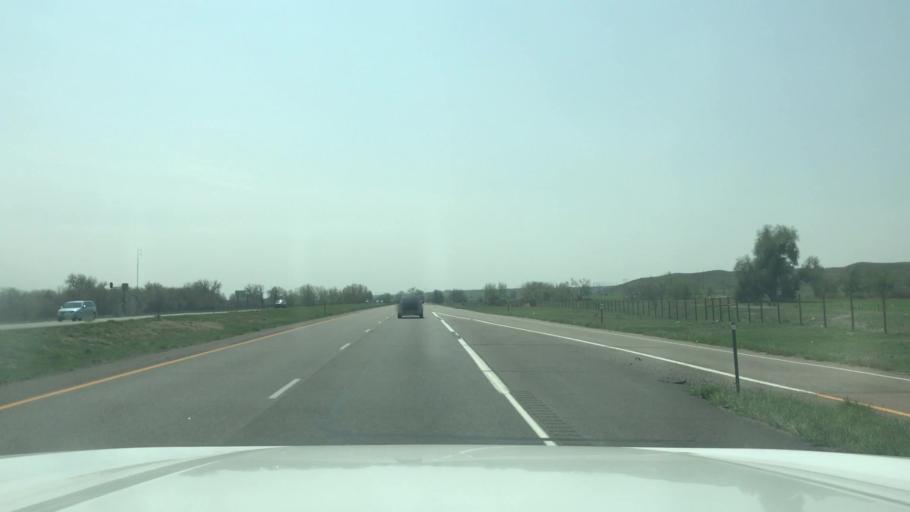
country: US
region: Colorado
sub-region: El Paso County
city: Fountain
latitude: 38.6260
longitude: -104.6903
